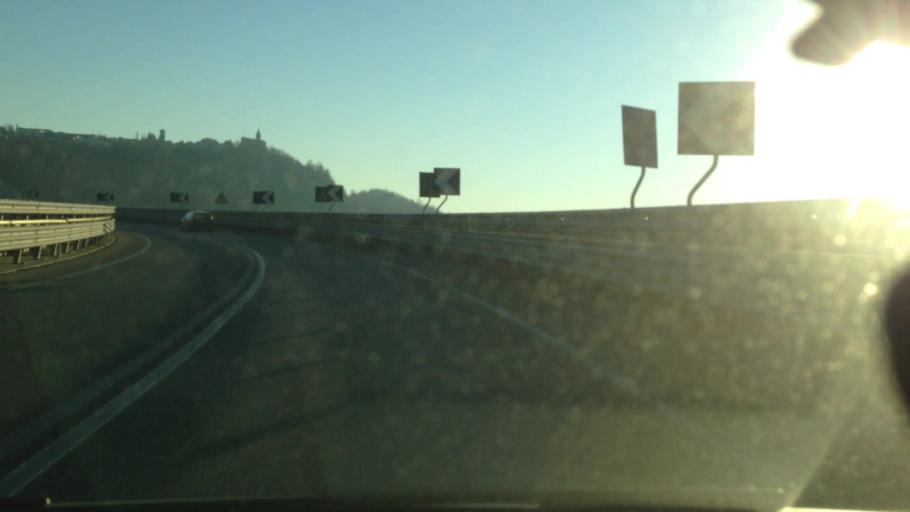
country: IT
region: Piedmont
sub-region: Provincia di Asti
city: Isola d'Asti
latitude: 44.8461
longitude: 8.1890
